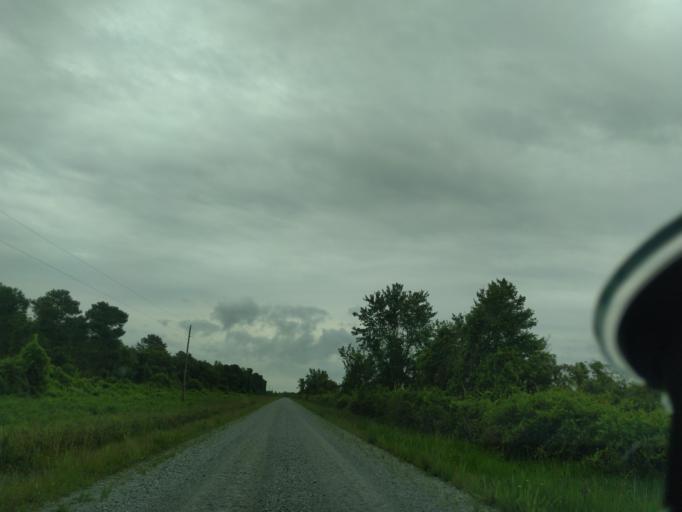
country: US
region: North Carolina
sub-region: Beaufort County
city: Belhaven
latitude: 35.7390
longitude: -76.4718
